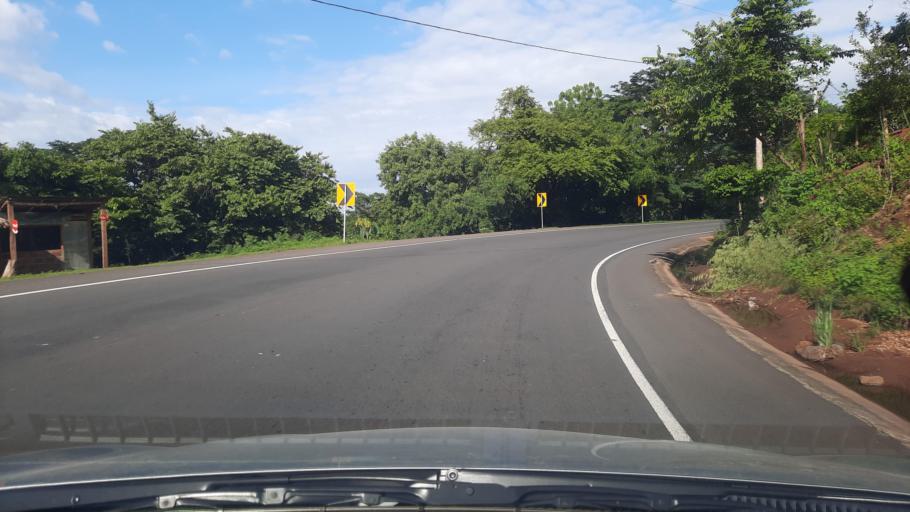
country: NI
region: Leon
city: Telica
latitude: 12.6952
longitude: -86.8592
